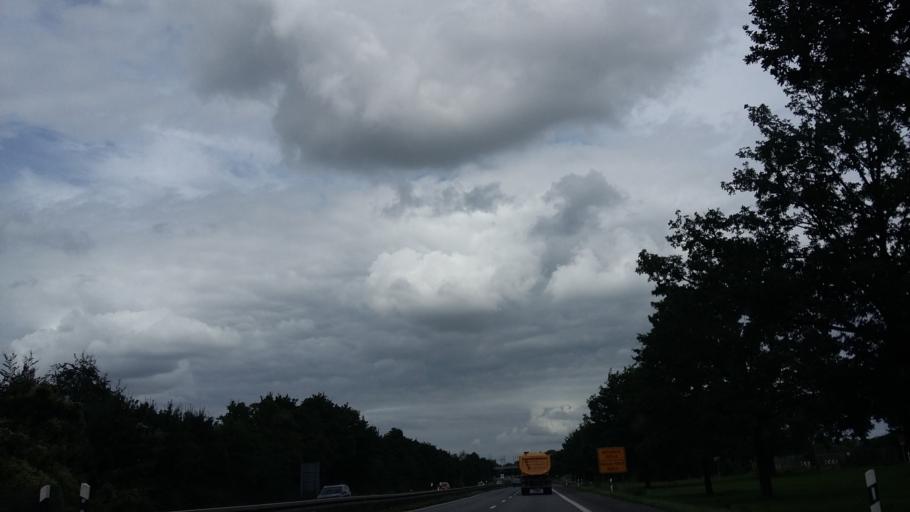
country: DE
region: Lower Saxony
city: Laatzen
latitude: 52.3242
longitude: 9.8133
